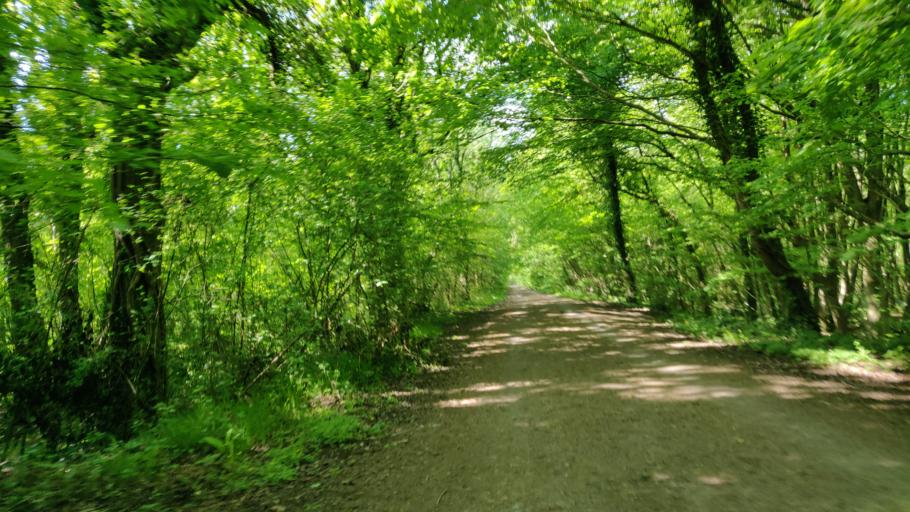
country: GB
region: England
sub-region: West Sussex
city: Rudgwick
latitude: 51.0749
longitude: -0.4274
